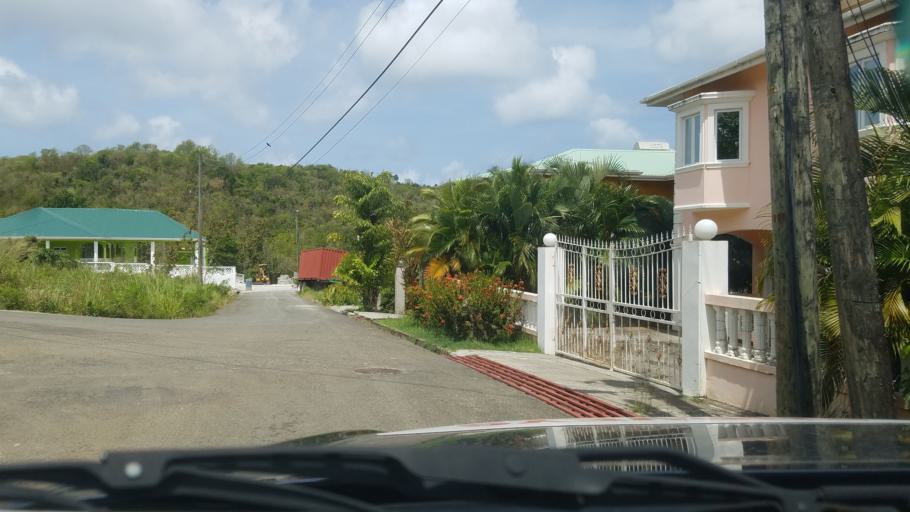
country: LC
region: Castries Quarter
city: Bisee
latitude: 14.0421
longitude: -60.9588
